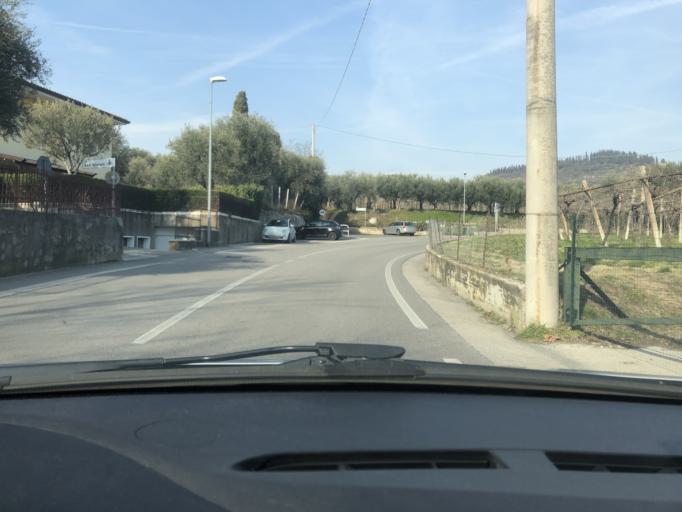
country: IT
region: Veneto
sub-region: Provincia di Verona
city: Bardolino
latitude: 45.5568
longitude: 10.7236
